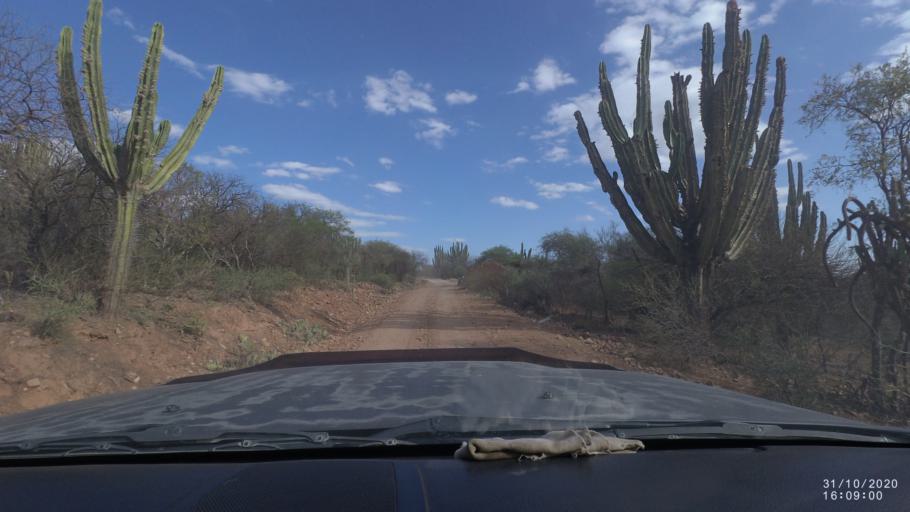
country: BO
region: Chuquisaca
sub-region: Provincia Zudanez
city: Mojocoya
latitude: -18.3862
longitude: -64.6386
